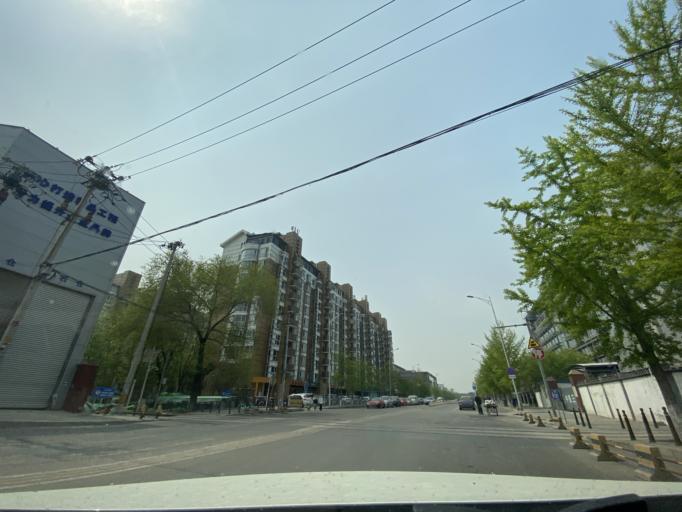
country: CN
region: Beijing
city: Sijiqing
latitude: 39.9400
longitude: 116.2676
